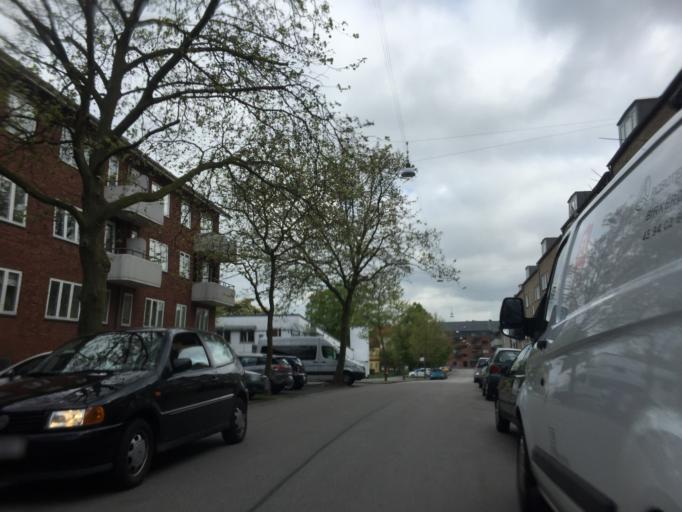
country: DK
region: Capital Region
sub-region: Frederiksberg Kommune
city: Frederiksberg
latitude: 55.7086
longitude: 12.5170
